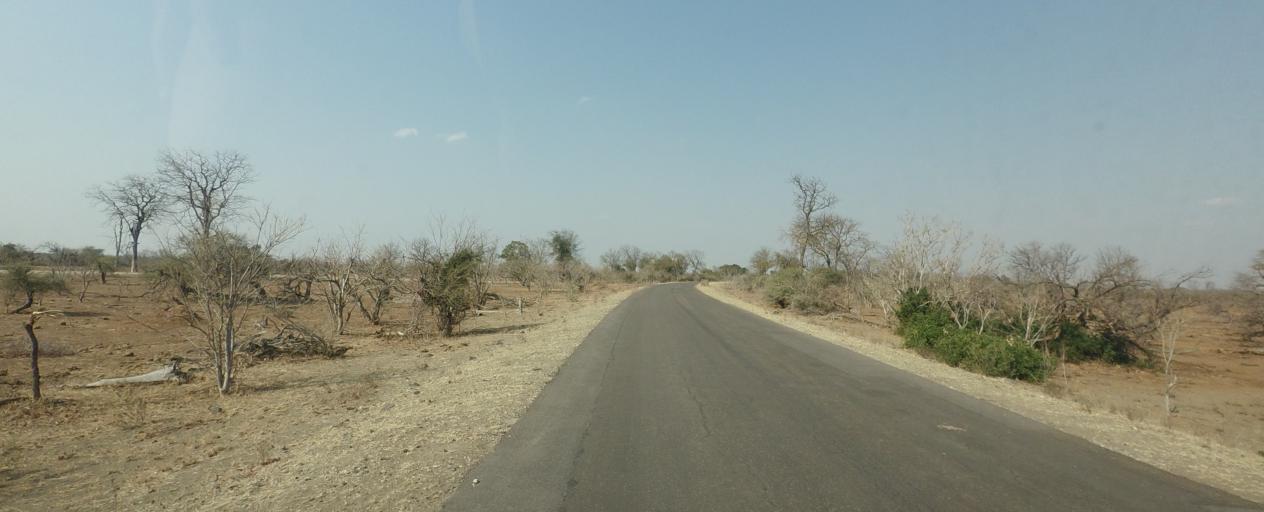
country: ZA
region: Limpopo
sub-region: Mopani District Municipality
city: Giyani
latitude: -23.0979
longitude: 31.3886
